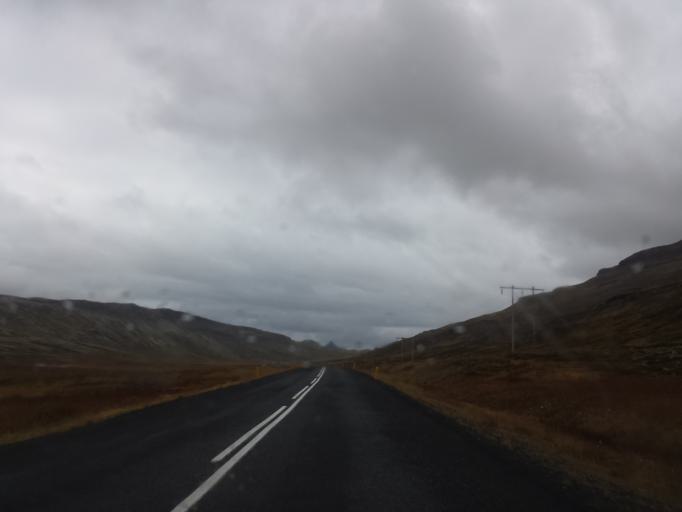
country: IS
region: West
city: Stykkisholmur
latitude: 64.8825
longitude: -22.8045
